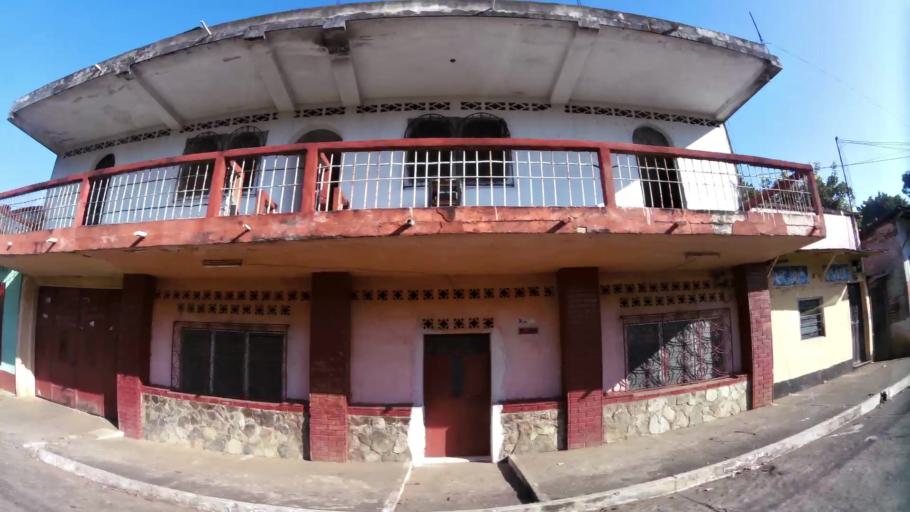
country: GT
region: Suchitepeque
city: Mazatenango
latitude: 14.5296
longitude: -91.5124
